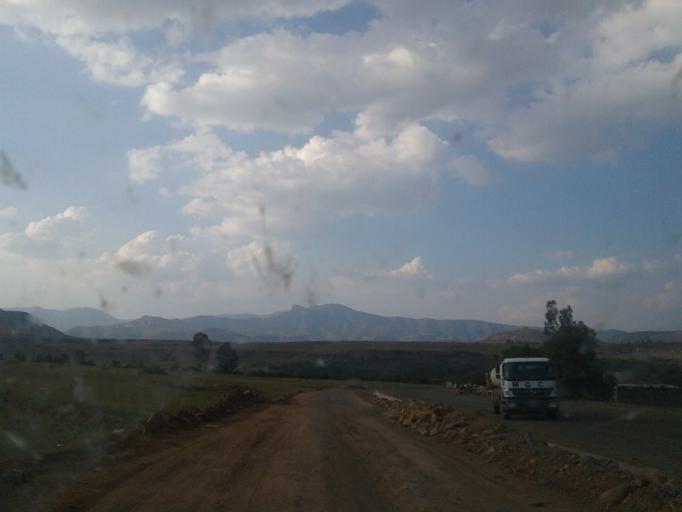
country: LS
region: Quthing
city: Quthing
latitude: -30.3976
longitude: 27.6122
